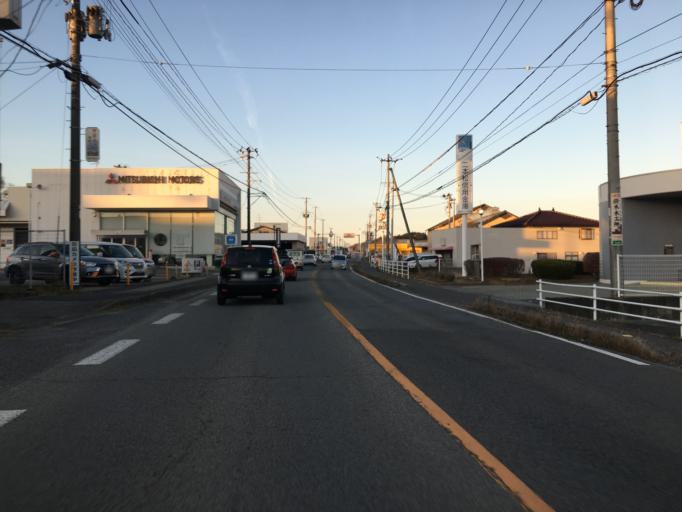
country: JP
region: Fukushima
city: Nihommatsu
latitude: 37.6061
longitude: 140.4603
